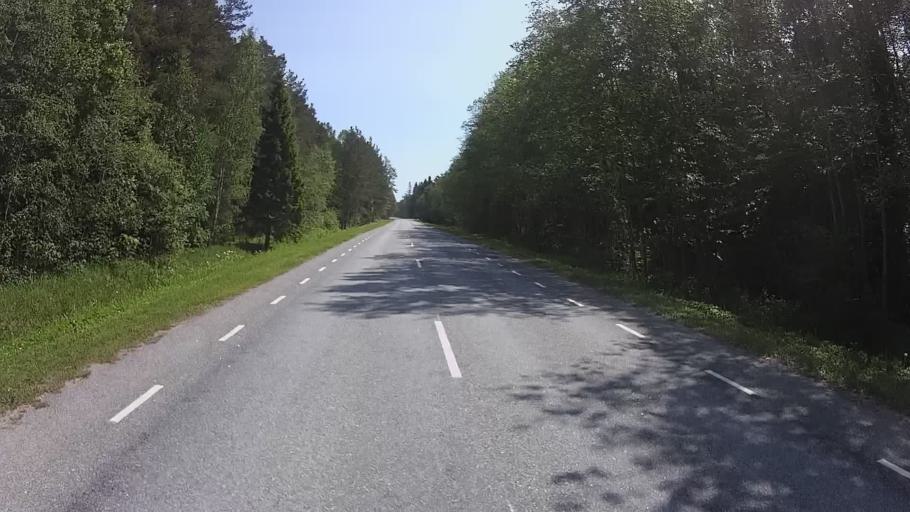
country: EE
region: Saare
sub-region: Kuressaare linn
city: Kuressaare
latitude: 58.3299
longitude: 22.2360
